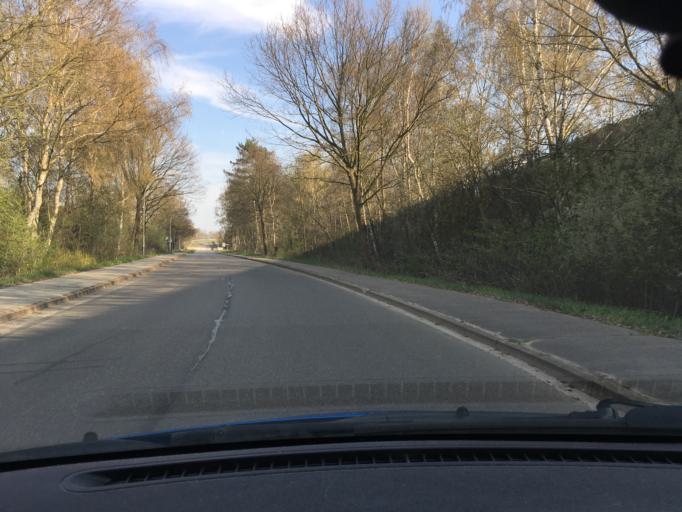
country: DE
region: Lower Saxony
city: Stelle
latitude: 53.4061
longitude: 10.0626
